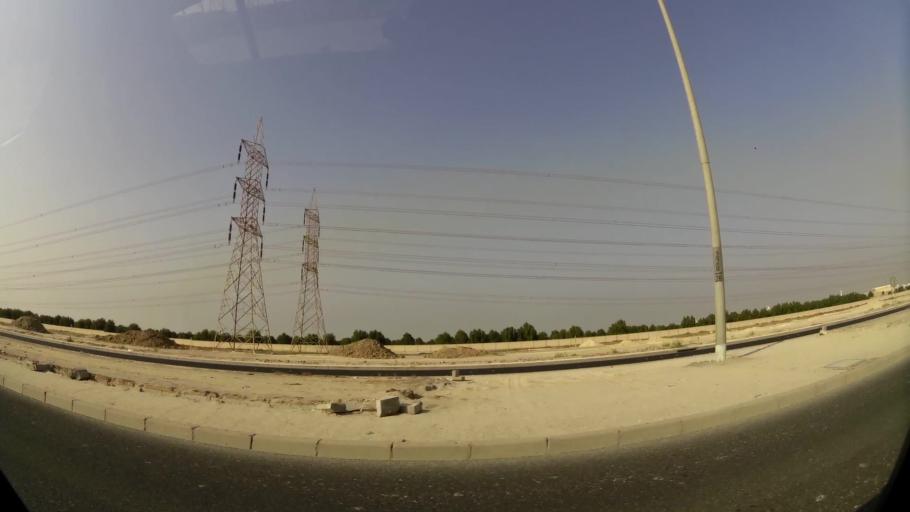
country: KW
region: Al Asimah
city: Ar Rabiyah
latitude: 29.2950
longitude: 47.8481
